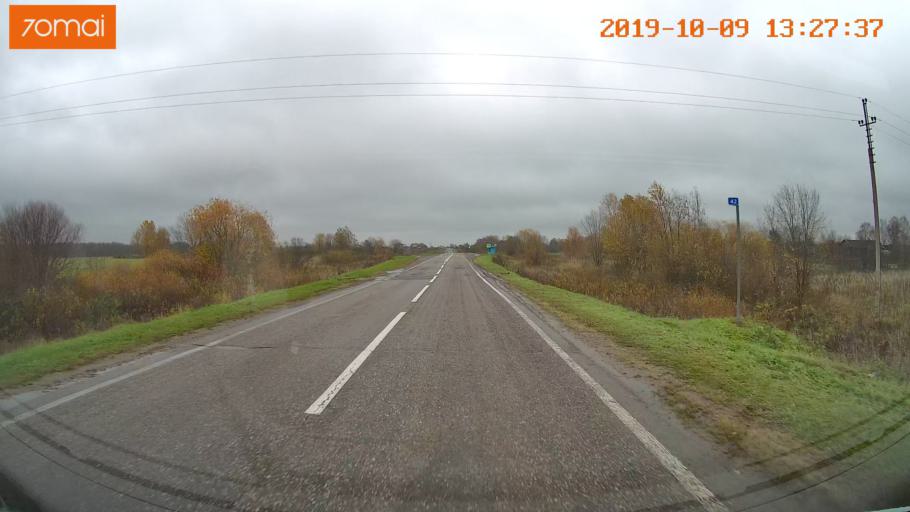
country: RU
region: Jaroslavl
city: Lyubim
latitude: 58.3153
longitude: 40.9504
